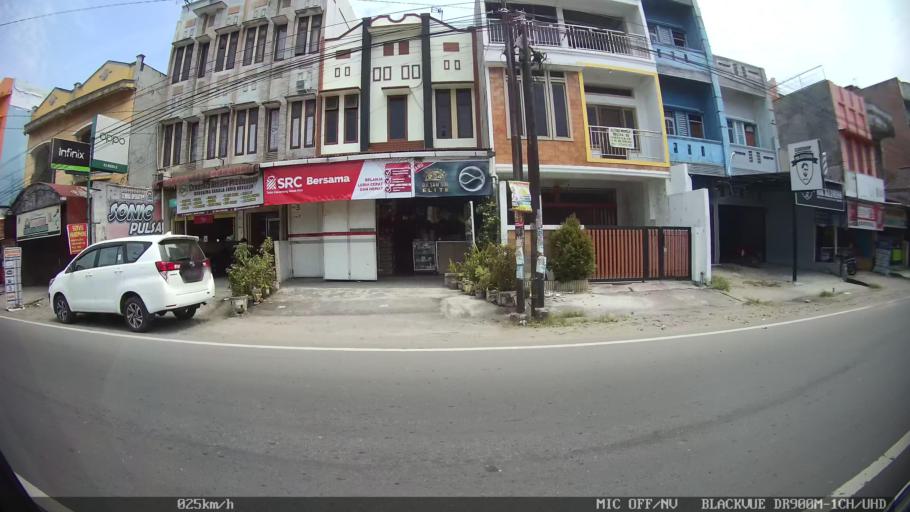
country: ID
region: North Sumatra
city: Sunggal
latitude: 3.5856
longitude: 98.6145
